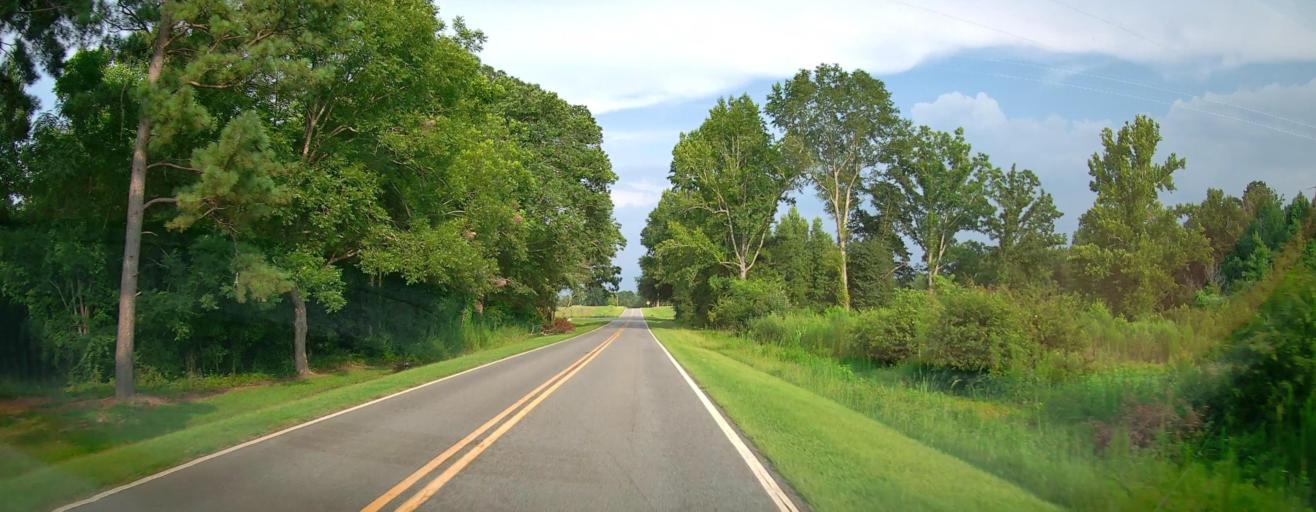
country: US
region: Georgia
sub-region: Laurens County
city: Dublin
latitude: 32.4835
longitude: -82.9698
